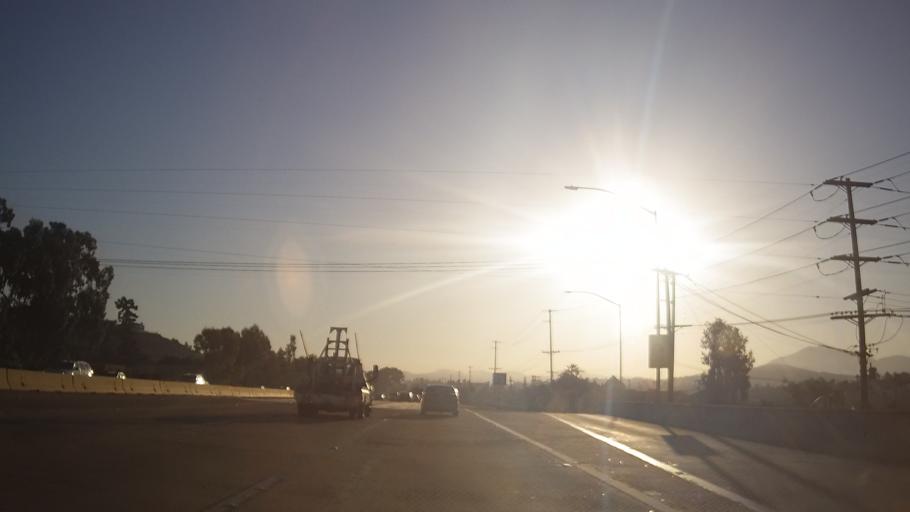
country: US
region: California
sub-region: San Diego County
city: Lemon Grove
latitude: 32.7447
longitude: -117.0432
